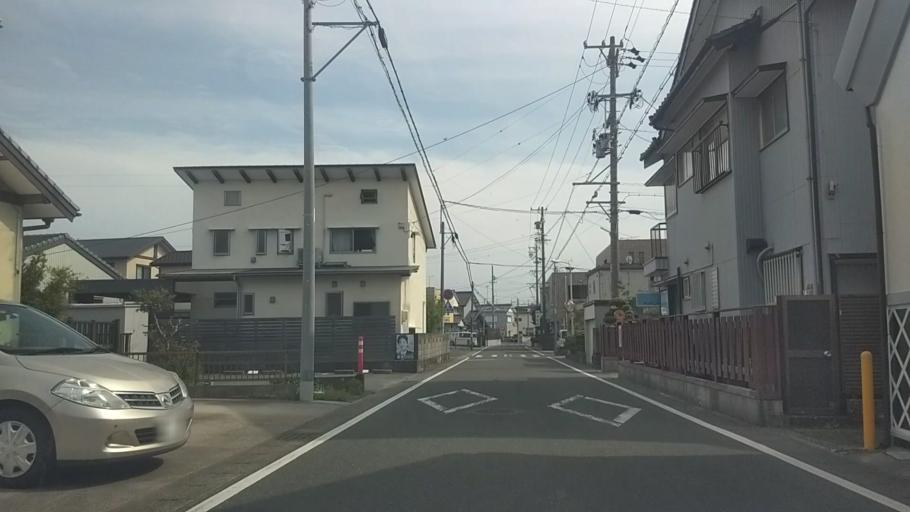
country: JP
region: Shizuoka
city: Kosai-shi
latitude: 34.7013
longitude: 137.6291
